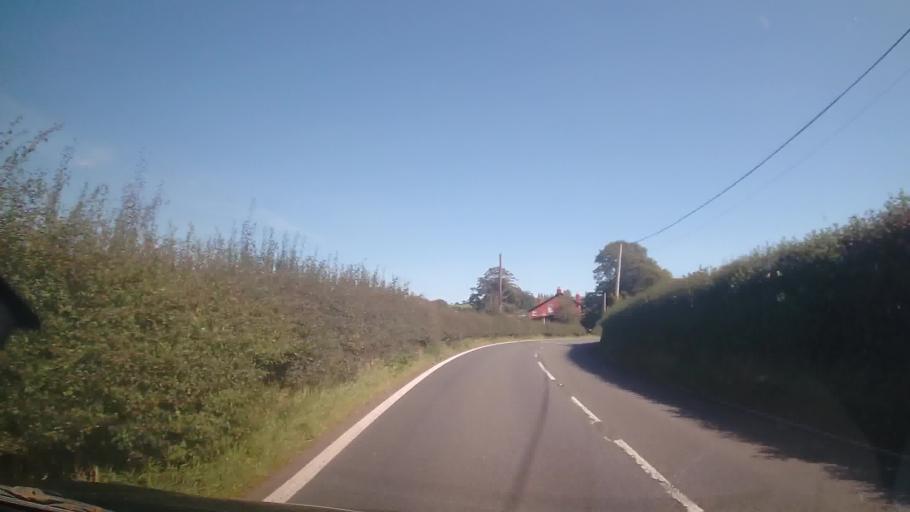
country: GB
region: Wales
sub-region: Sir Powys
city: Mochdre
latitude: 52.4796
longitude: -3.3287
